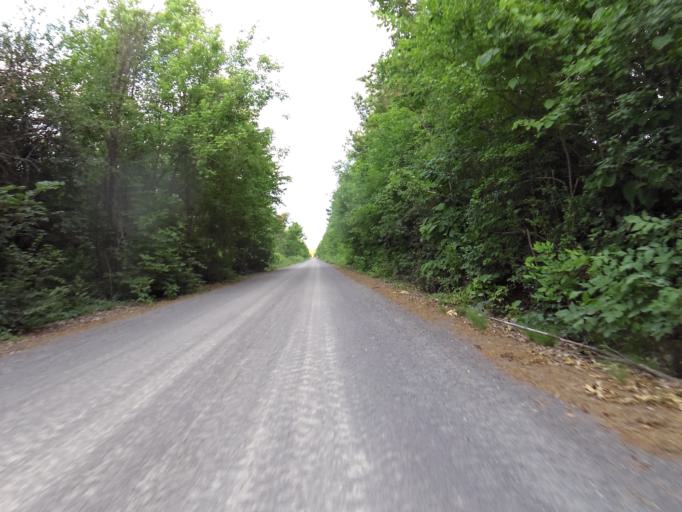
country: CA
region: Ontario
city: Arnprior
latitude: 45.3378
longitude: -76.2966
